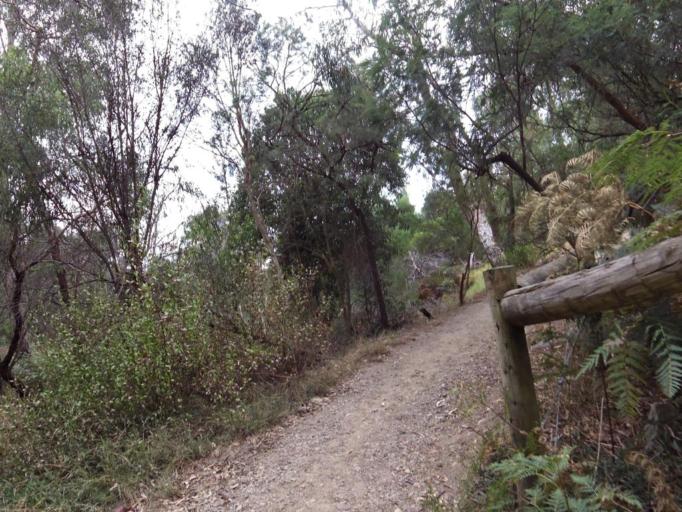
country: AU
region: Victoria
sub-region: Frankston
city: Frankston
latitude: -38.1629
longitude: 145.1116
